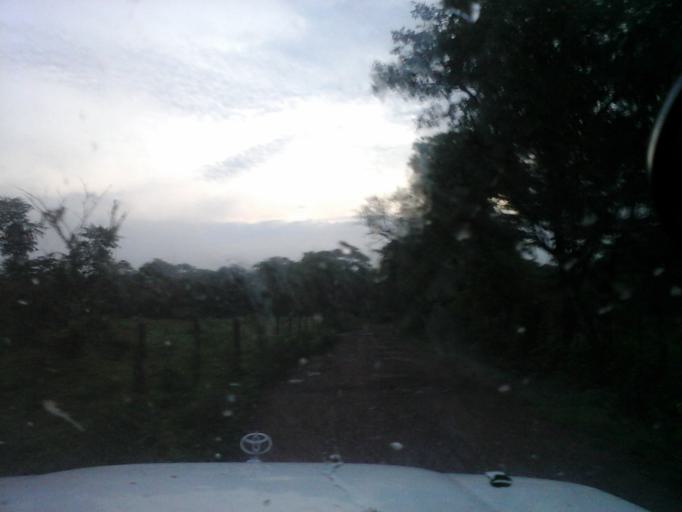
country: CO
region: Cesar
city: Agustin Codazzi
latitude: 10.1621
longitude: -73.2005
